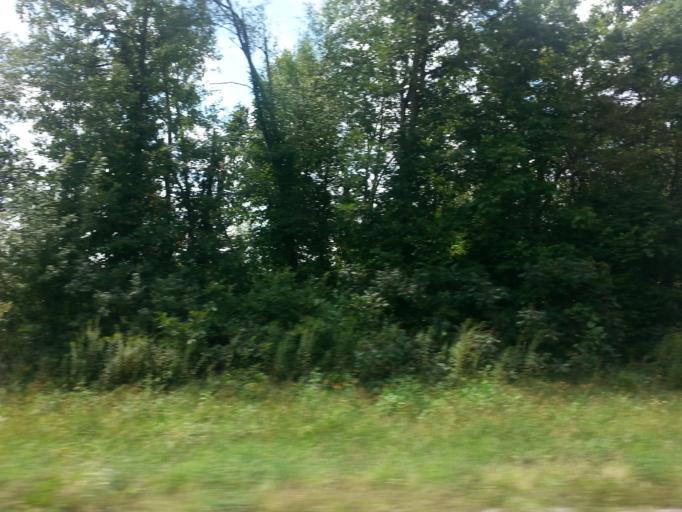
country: US
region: Tennessee
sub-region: Cumberland County
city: Crossville
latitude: 36.0194
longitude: -85.0757
